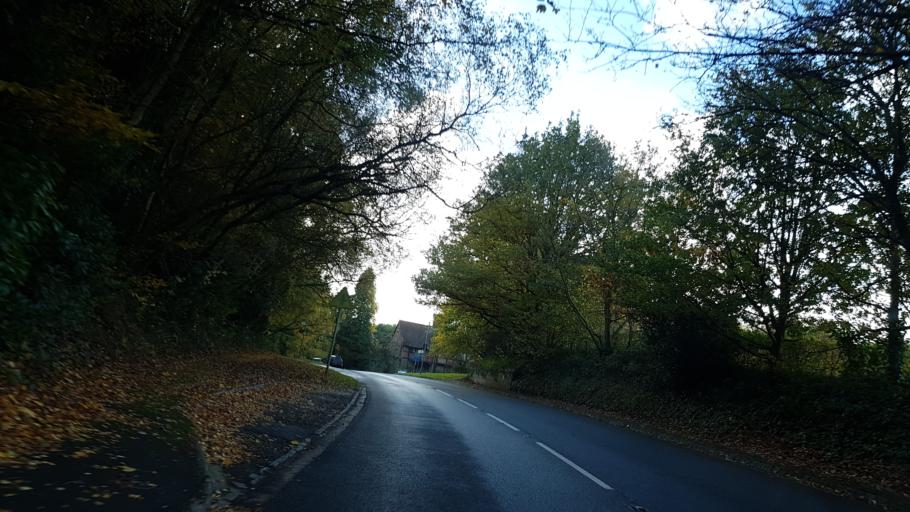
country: GB
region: England
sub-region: Surrey
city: Milford
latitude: 51.1330
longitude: -0.6727
